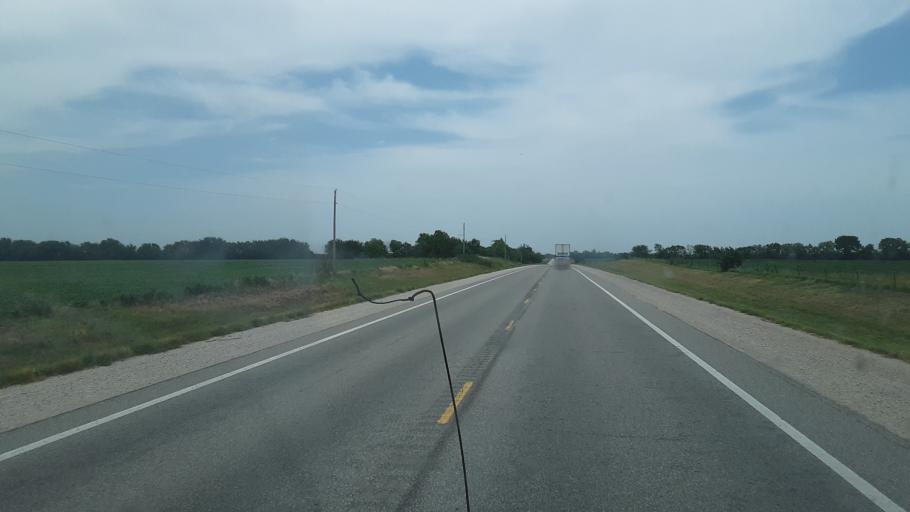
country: US
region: Kansas
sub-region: Allen County
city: Iola
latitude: 37.9216
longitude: -95.2204
